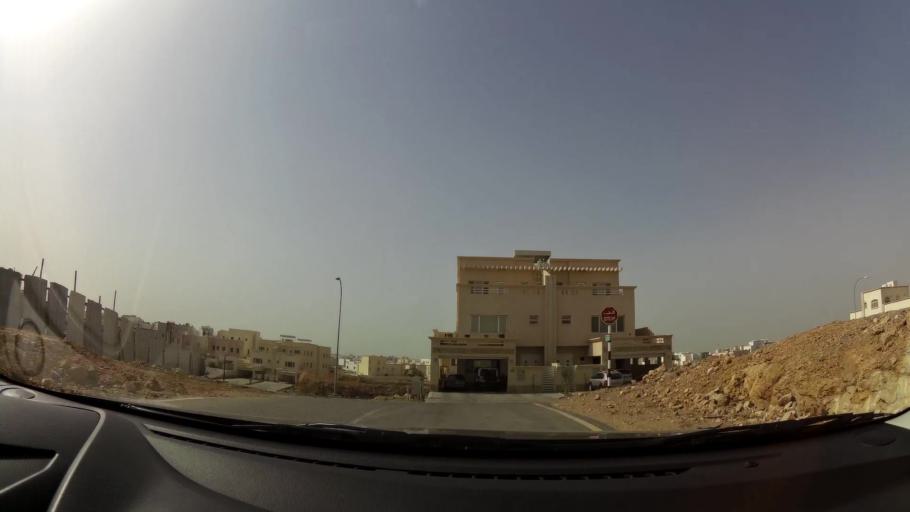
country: OM
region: Muhafazat Masqat
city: Bawshar
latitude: 23.5500
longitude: 58.3504
